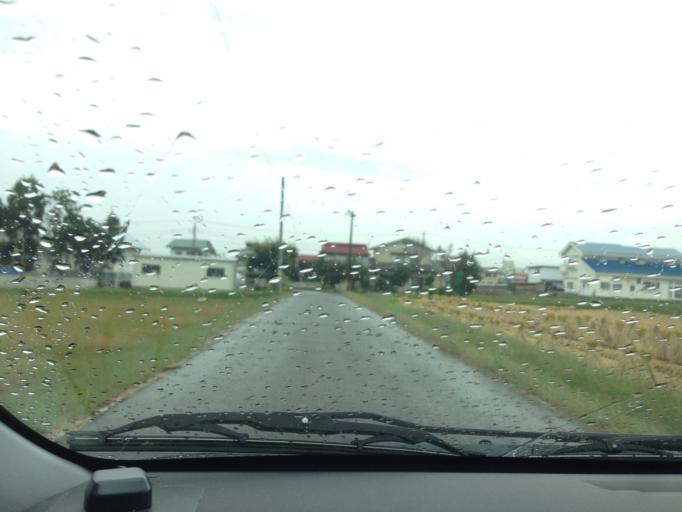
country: JP
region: Fukushima
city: Kitakata
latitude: 37.5207
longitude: 139.8306
